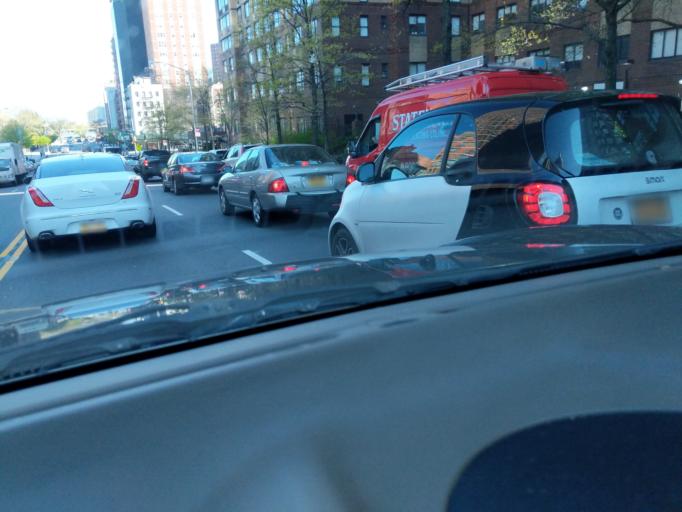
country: US
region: New York
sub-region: New York County
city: Manhattan
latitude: 40.7849
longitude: -73.9488
